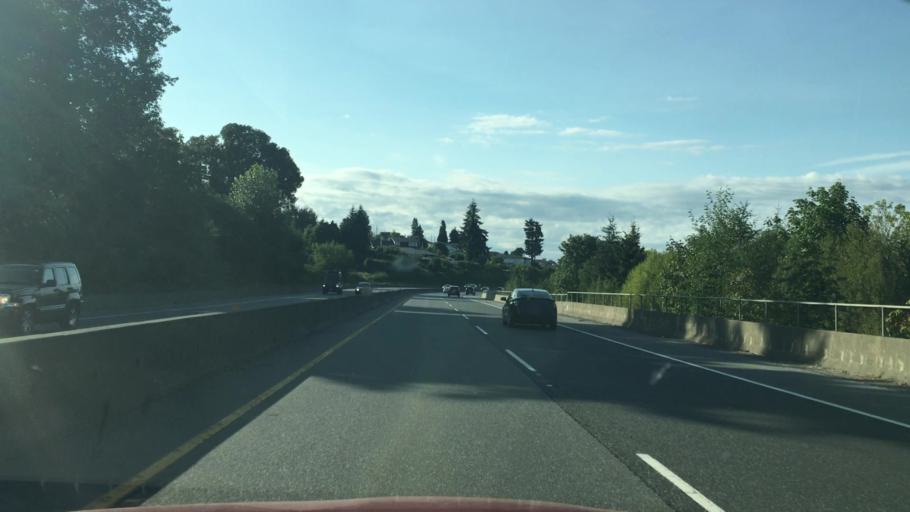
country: CA
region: British Columbia
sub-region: Cowichan Valley Regional District
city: Ladysmith
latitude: 48.9853
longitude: -123.8073
